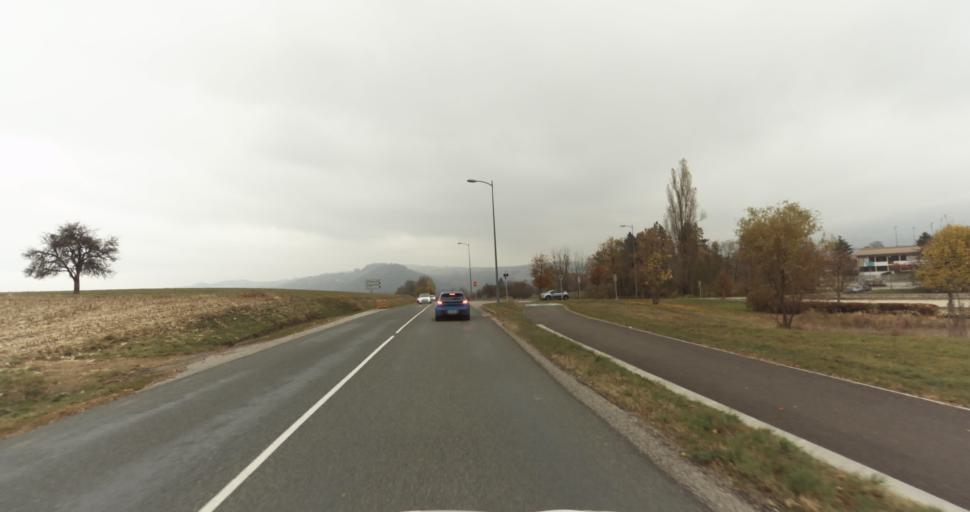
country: FR
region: Rhone-Alpes
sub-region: Departement de la Haute-Savoie
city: Alby-sur-Cheran
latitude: 45.8053
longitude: 6.0114
